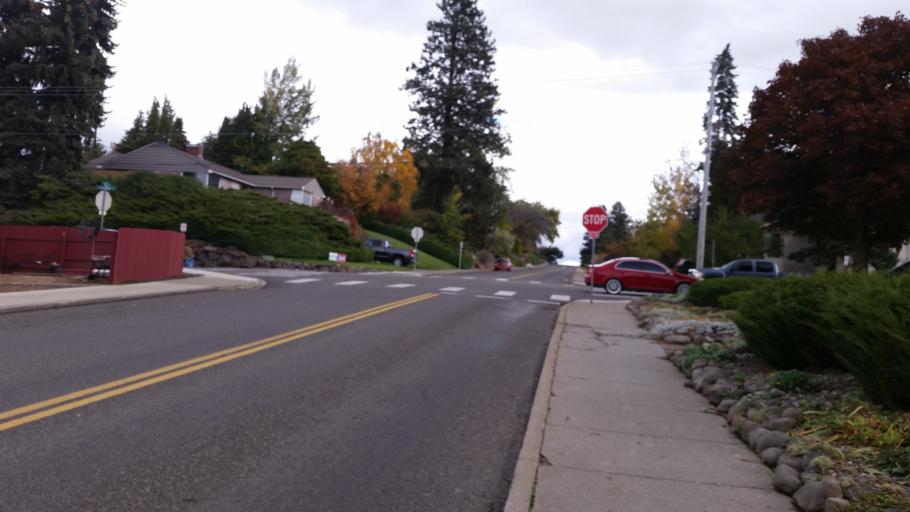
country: US
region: Washington
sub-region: Kittitas County
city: Ellensburg
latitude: 46.9946
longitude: -120.5376
